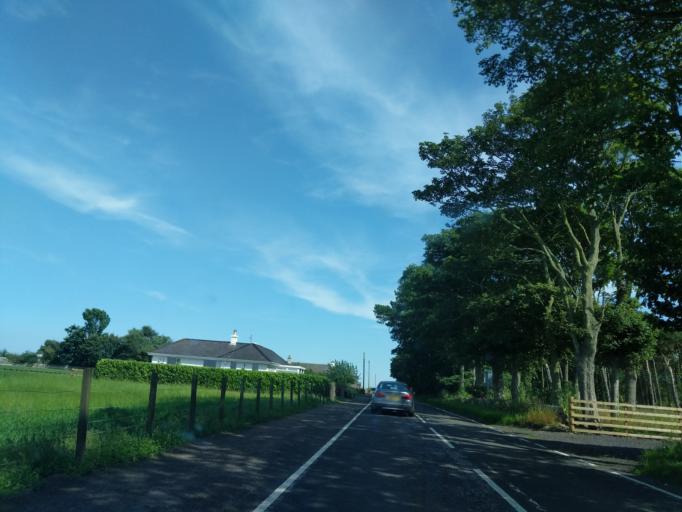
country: GB
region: Scotland
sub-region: Fife
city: Saint Andrews
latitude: 56.3270
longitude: -2.7696
